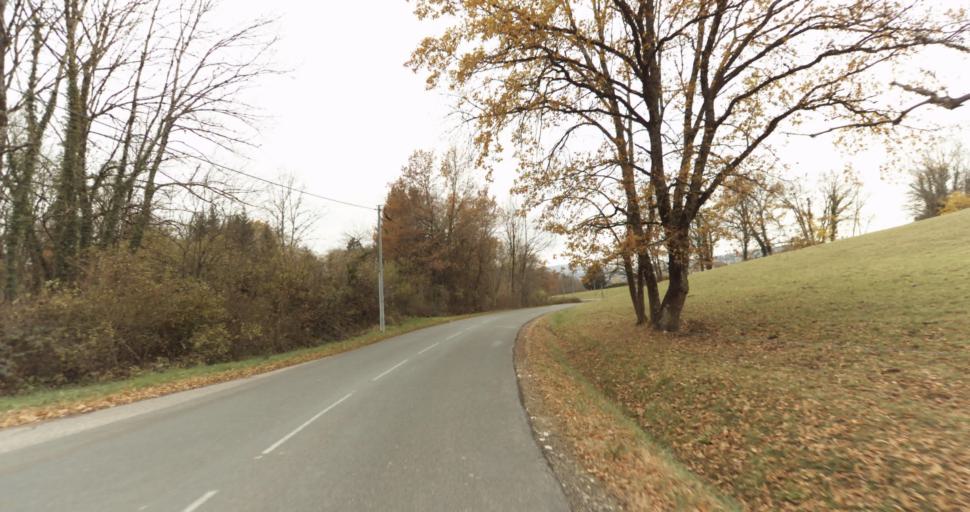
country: FR
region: Rhone-Alpes
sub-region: Departement de la Haute-Savoie
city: Saint-Martin-Bellevue
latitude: 45.9648
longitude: 6.1453
